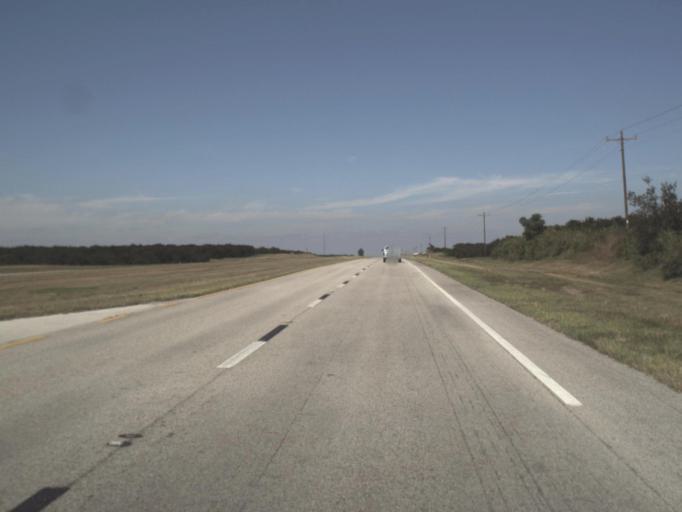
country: US
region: Florida
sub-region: Highlands County
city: Placid Lakes
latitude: 27.1790
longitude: -81.3285
